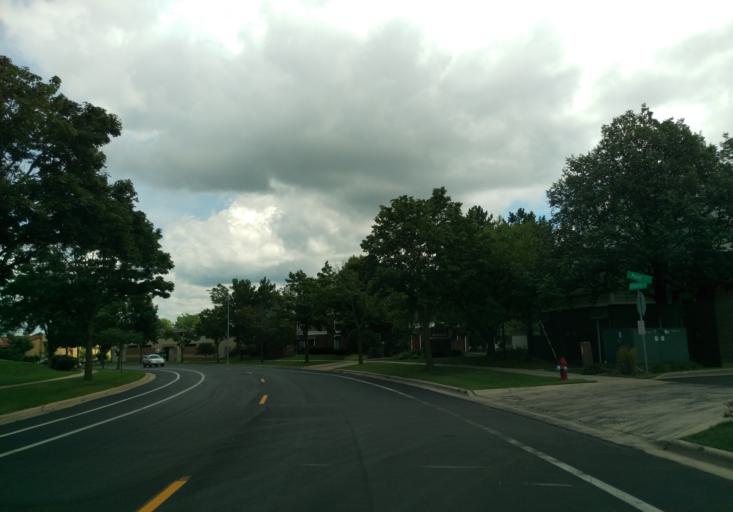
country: US
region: Wisconsin
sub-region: Dane County
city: Middleton
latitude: 43.0569
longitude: -89.5157
